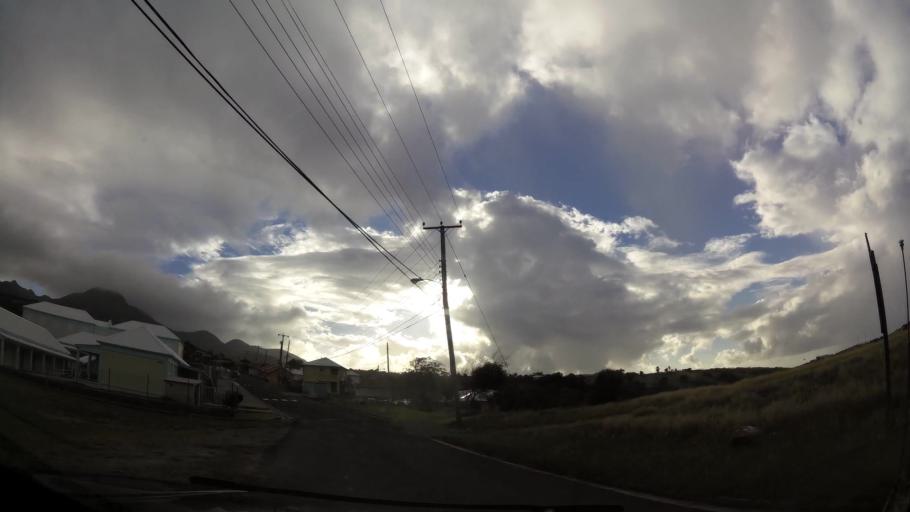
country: MS
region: Saint Peter
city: Brades
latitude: 16.7905
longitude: -62.1877
